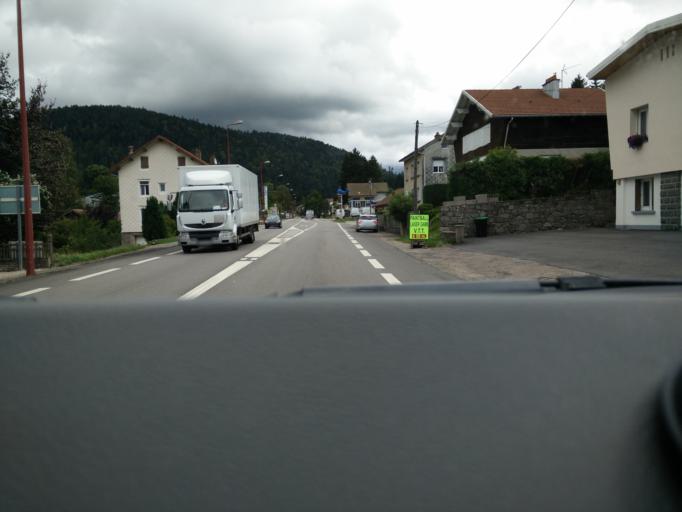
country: FR
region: Lorraine
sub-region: Departement des Vosges
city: Gerardmer
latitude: 48.0804
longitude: 6.8955
